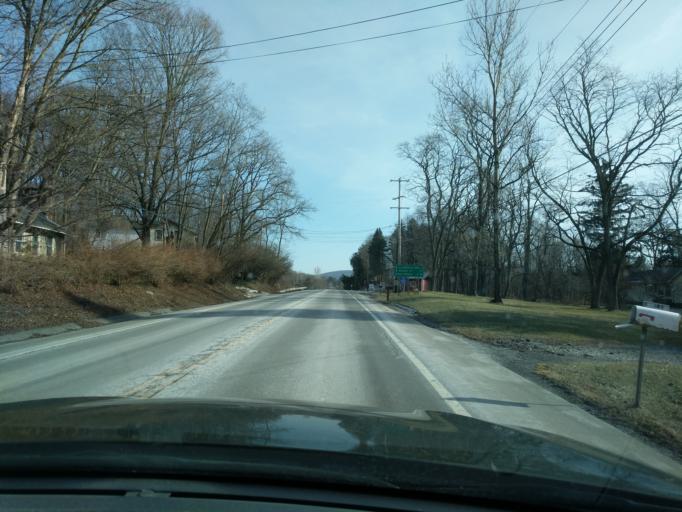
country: US
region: New York
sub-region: Tompkins County
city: East Ithaca
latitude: 42.4034
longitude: -76.4255
